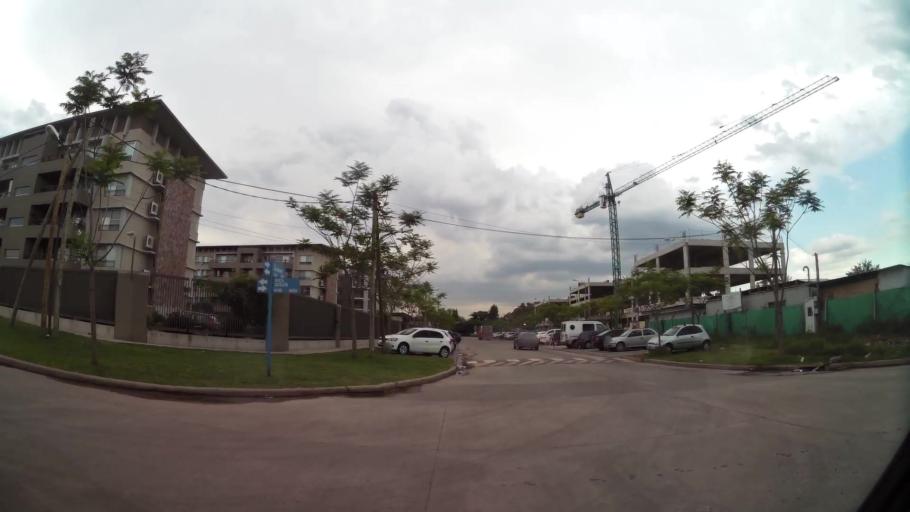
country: AR
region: Buenos Aires
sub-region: Partido de Tigre
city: Tigre
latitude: -34.4820
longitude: -58.5897
